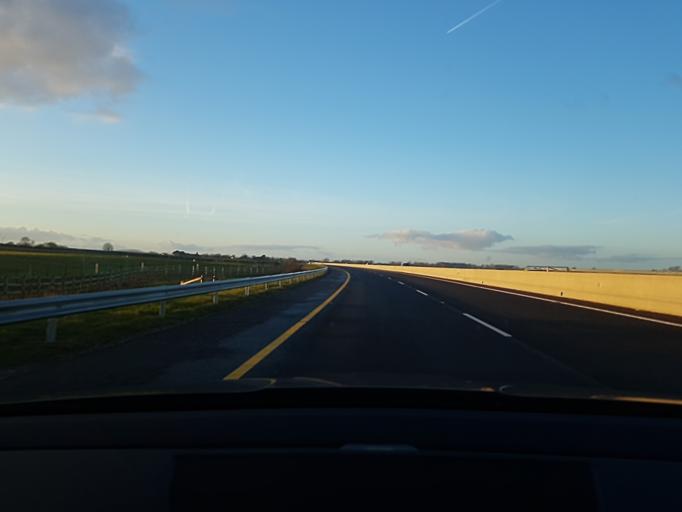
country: IE
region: Connaught
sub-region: County Galway
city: Tuam
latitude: 53.4241
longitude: -8.8316
